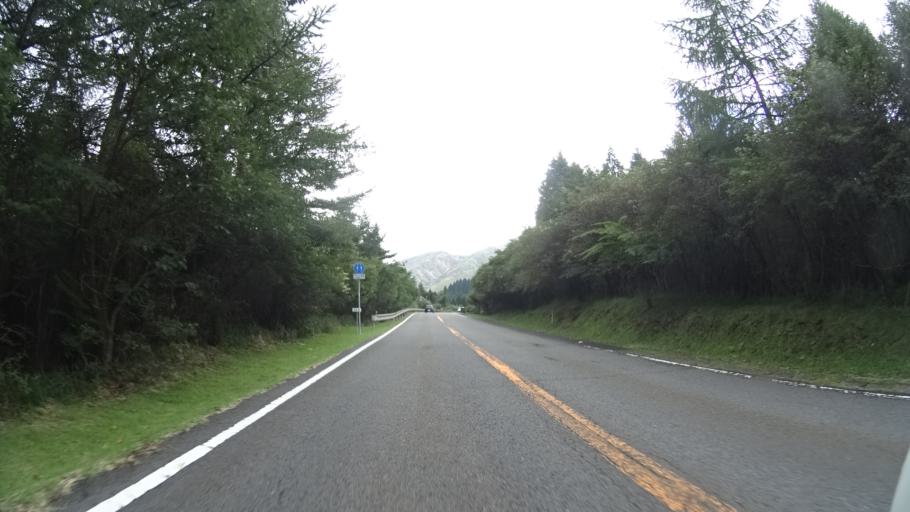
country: JP
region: Oita
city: Tsukawaki
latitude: 33.1044
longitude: 131.2204
